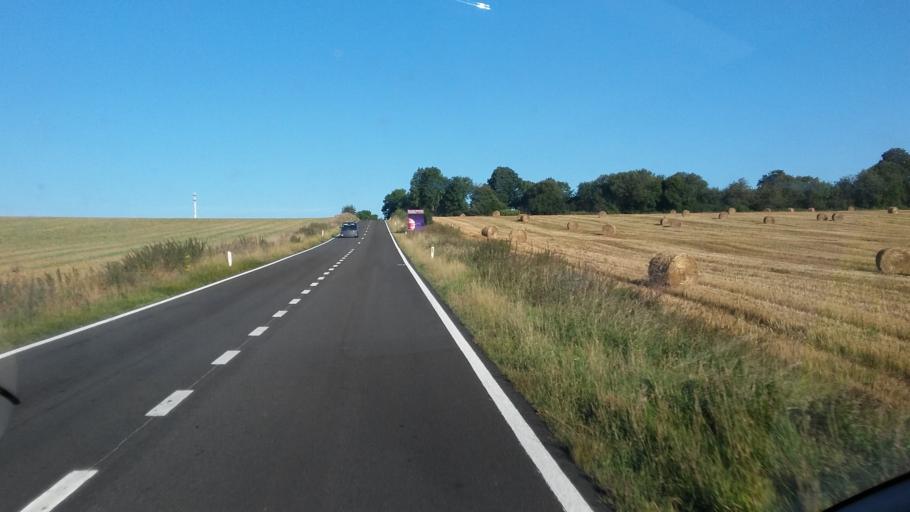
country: BE
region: Wallonia
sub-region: Province du Luxembourg
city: Leglise
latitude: 49.8230
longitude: 5.4911
